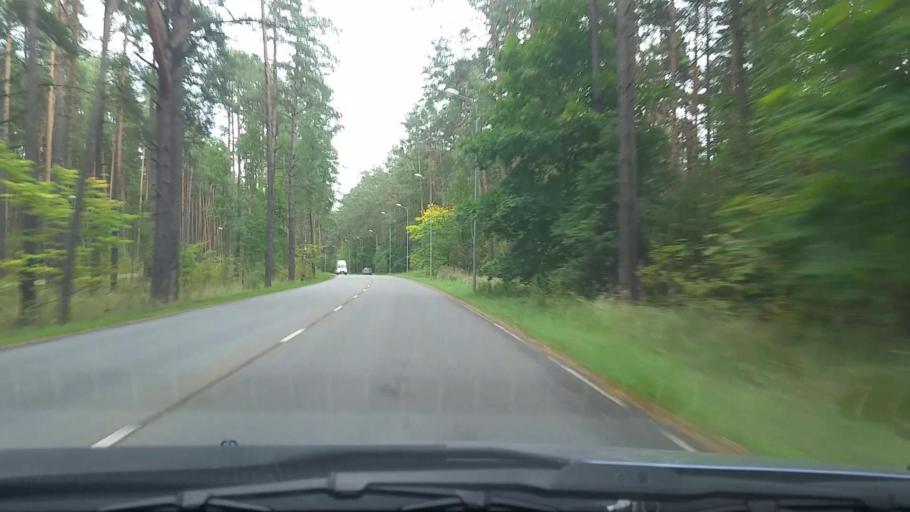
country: LV
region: Riga
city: Jaunciems
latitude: 56.9771
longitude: 24.2174
